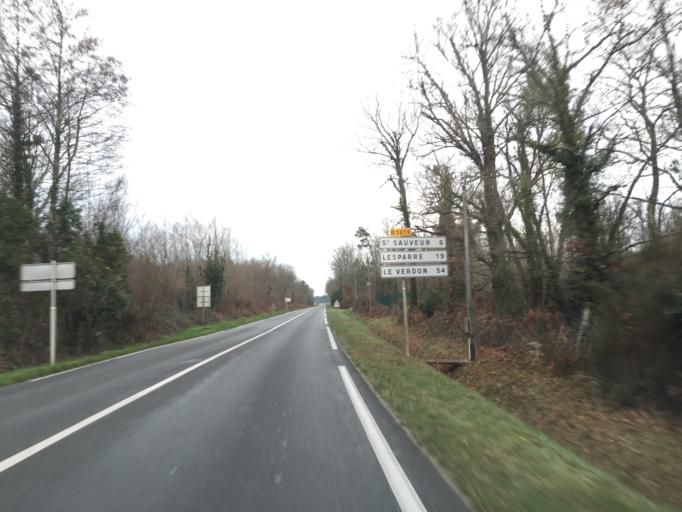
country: FR
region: Aquitaine
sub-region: Departement de la Gironde
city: Saint-Sauveur
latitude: 45.1625
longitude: -0.8299
